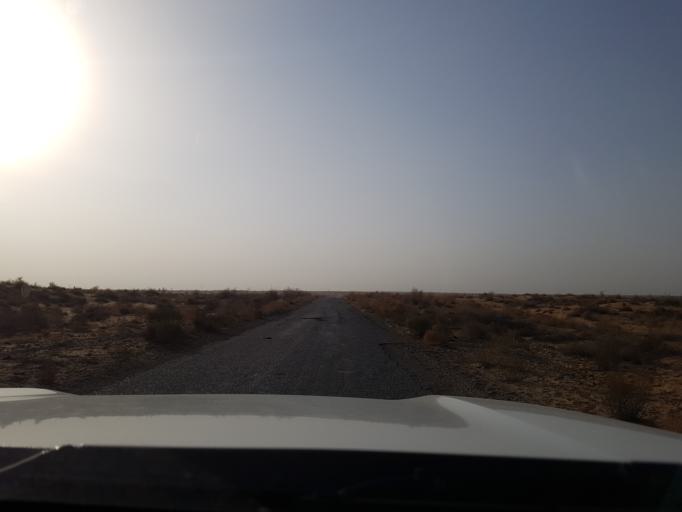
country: UZ
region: Xorazm
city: Hazorasp
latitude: 41.1928
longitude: 60.9051
